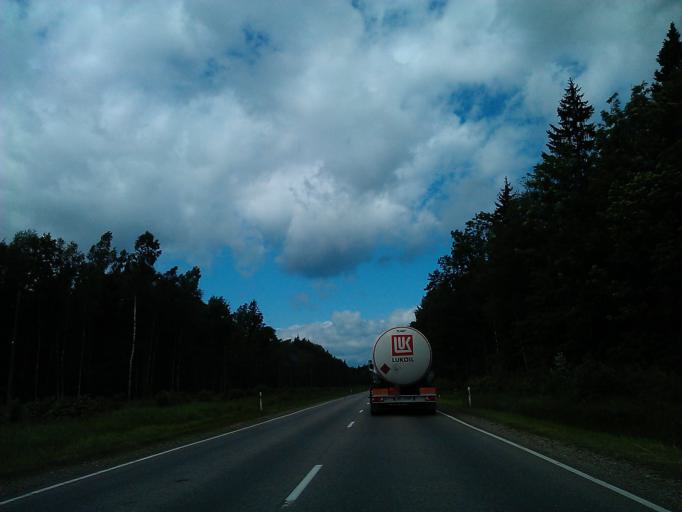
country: LV
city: Tireli
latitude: 56.9316
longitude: 23.4997
